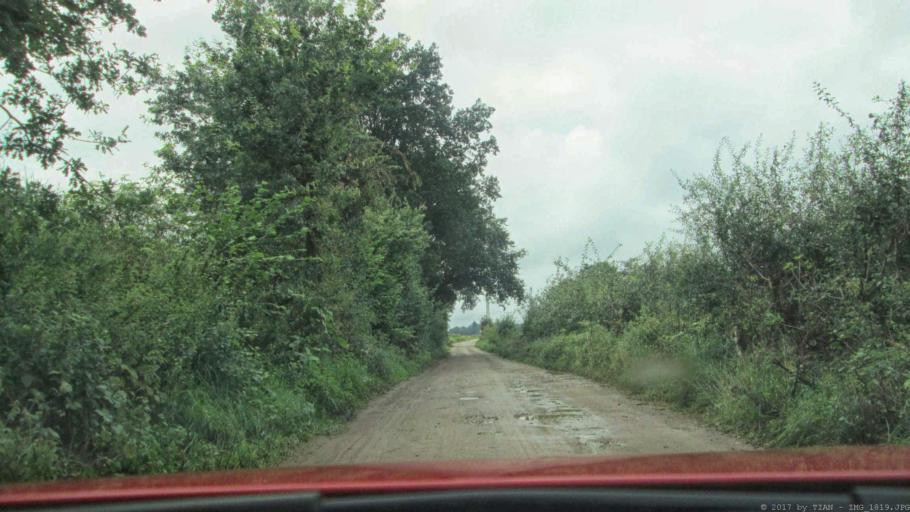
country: DE
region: Lower Saxony
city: Emmendorf
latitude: 53.0456
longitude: 10.5694
